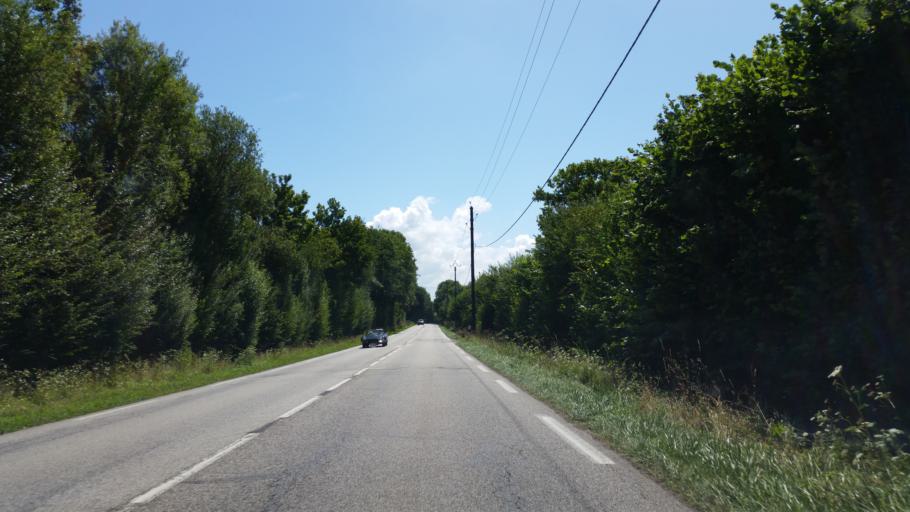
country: FR
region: Lower Normandy
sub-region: Departement du Calvados
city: Saint-Gatien-des-Bois
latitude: 49.3420
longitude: 0.2032
